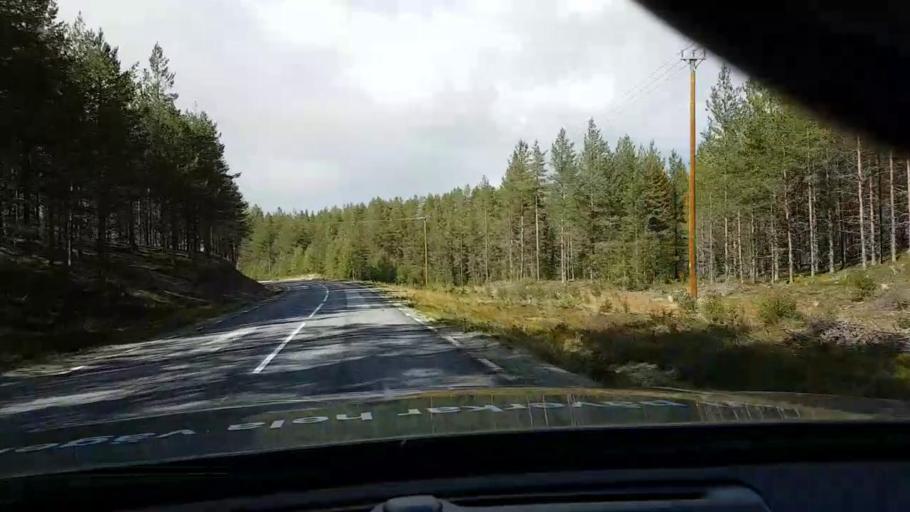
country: SE
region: Vaesterbotten
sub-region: Asele Kommun
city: Asele
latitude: 63.8530
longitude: 17.3926
